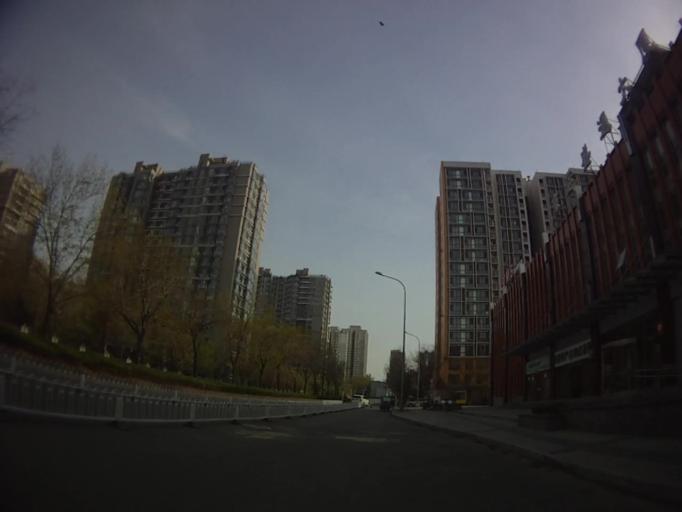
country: CN
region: Beijing
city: Longtan
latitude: 39.8955
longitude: 116.4441
